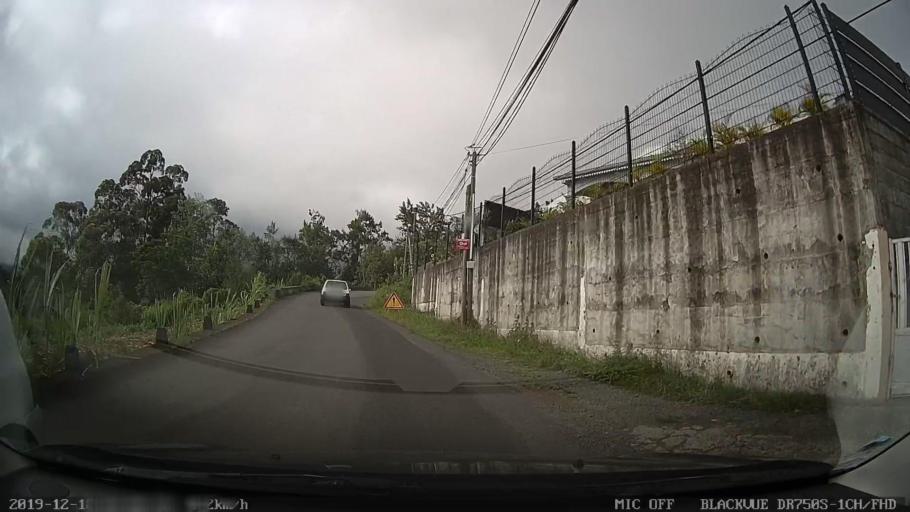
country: RE
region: Reunion
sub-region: Reunion
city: Le Tampon
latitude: -21.2530
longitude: 55.5181
